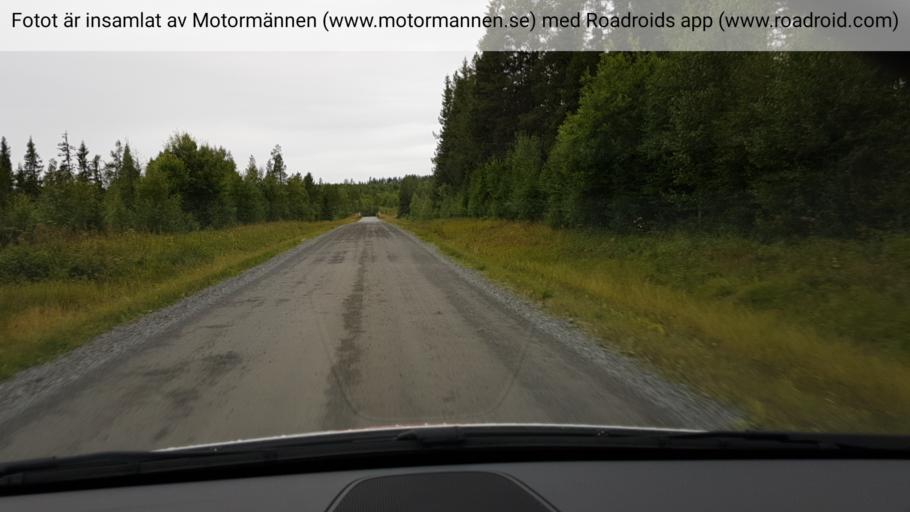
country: SE
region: Jaemtland
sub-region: OEstersunds Kommun
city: Lit
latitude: 63.6788
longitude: 14.7521
